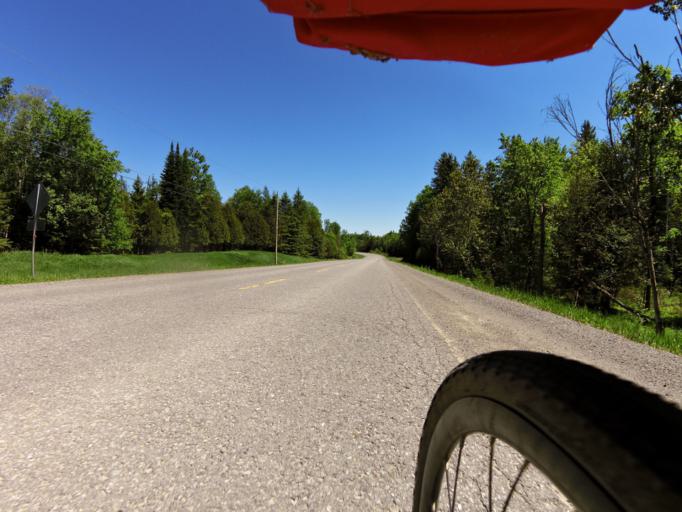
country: CA
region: Ontario
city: Carleton Place
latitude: 45.1837
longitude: -76.3890
